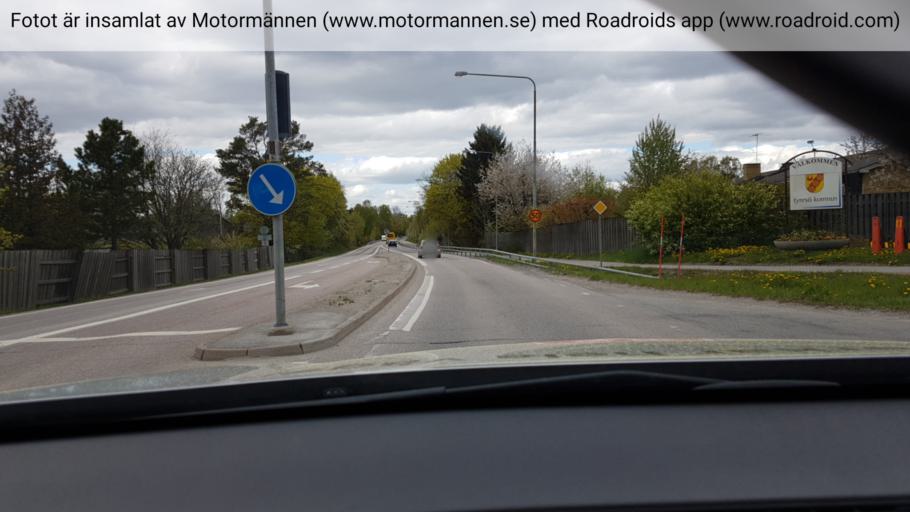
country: SE
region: Stockholm
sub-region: Tyreso Kommun
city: Bollmora
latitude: 59.2141
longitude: 18.2082
